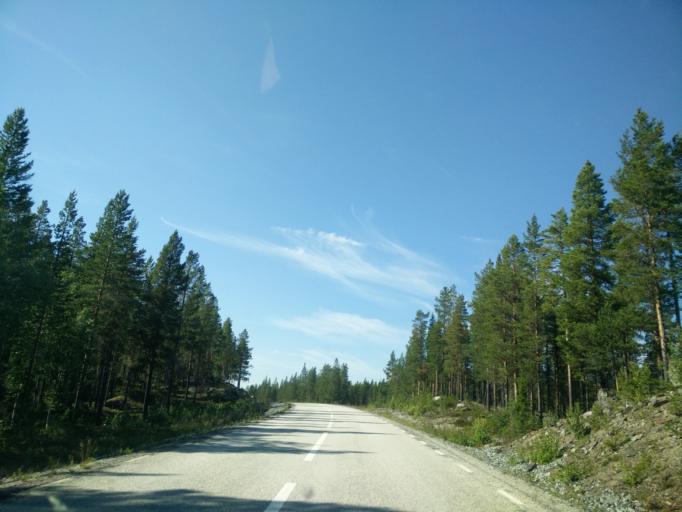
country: SE
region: Jaemtland
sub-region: Are Kommun
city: Jarpen
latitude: 62.8305
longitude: 13.4504
